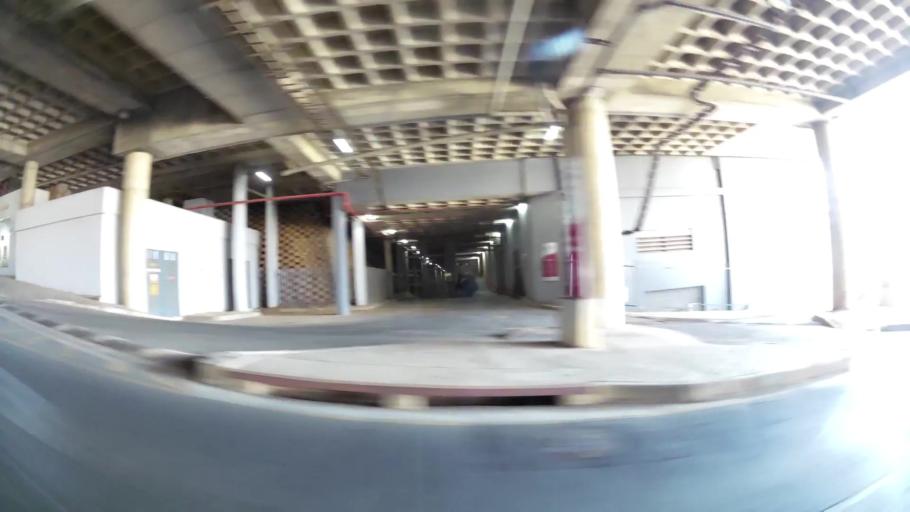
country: ZA
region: Gauteng
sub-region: City of Johannesburg Metropolitan Municipality
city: Modderfontein
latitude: -26.1167
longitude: 28.1455
